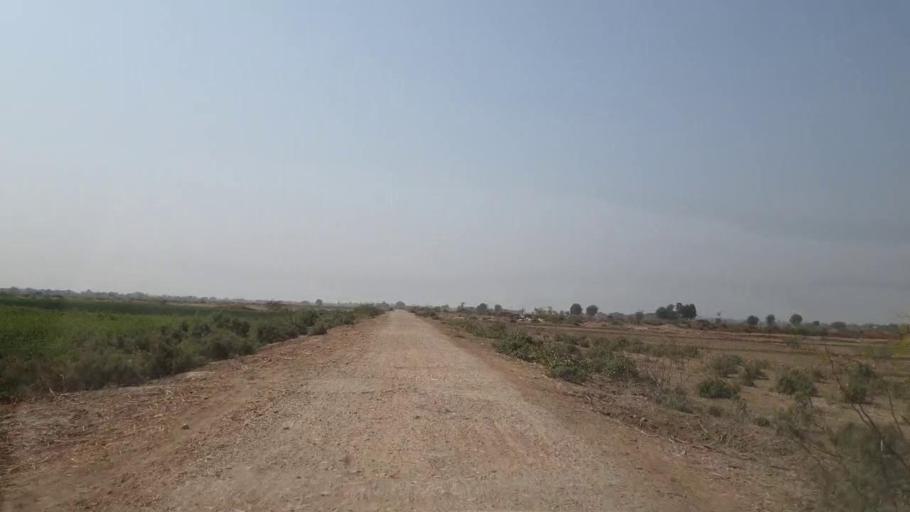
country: PK
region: Sindh
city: Mirpur Khas
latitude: 25.6559
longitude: 69.1287
